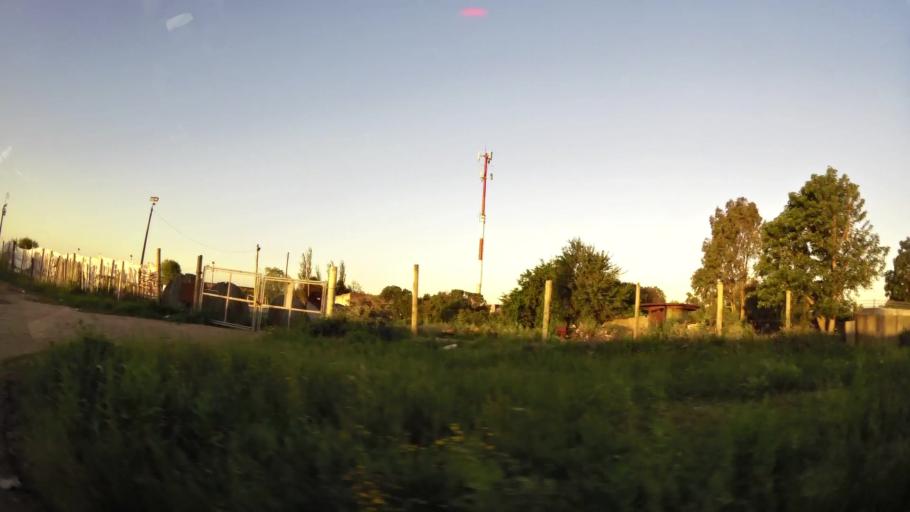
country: UY
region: Montevideo
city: Montevideo
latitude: -34.8281
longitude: -56.1561
